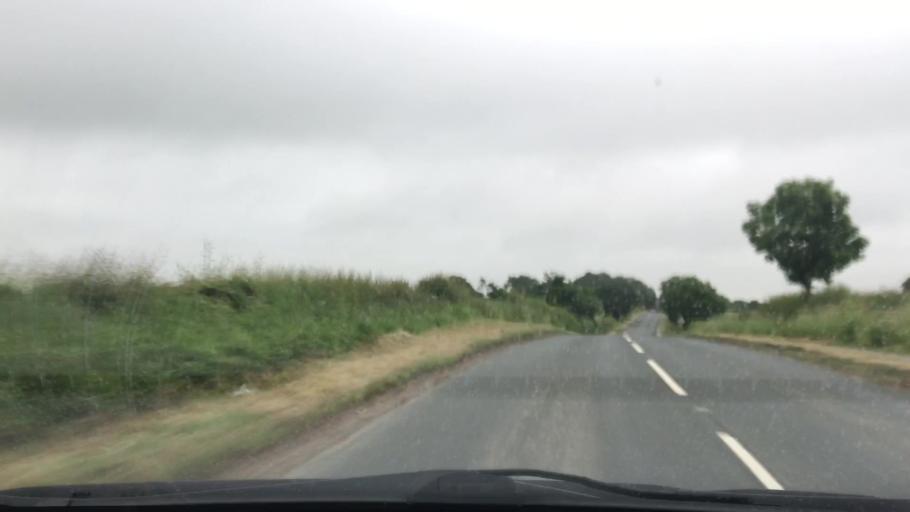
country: GB
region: England
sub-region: City and Borough of Leeds
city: Wetherby
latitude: 53.9566
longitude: -1.4014
